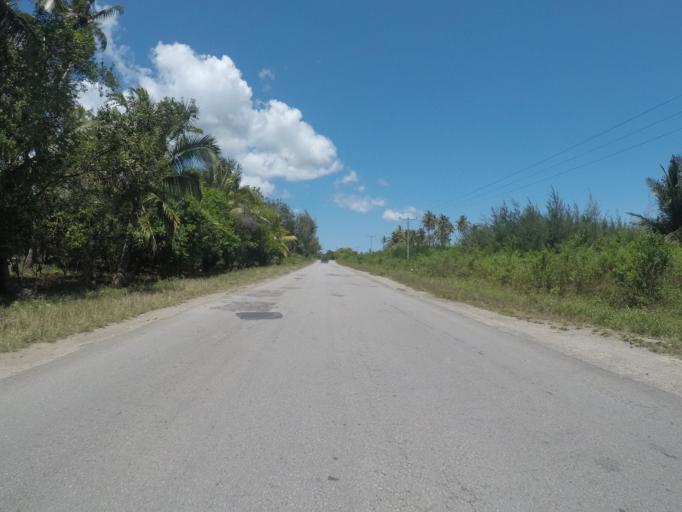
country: TZ
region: Zanzibar Central/South
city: Nganane
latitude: -6.2746
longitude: 39.4303
